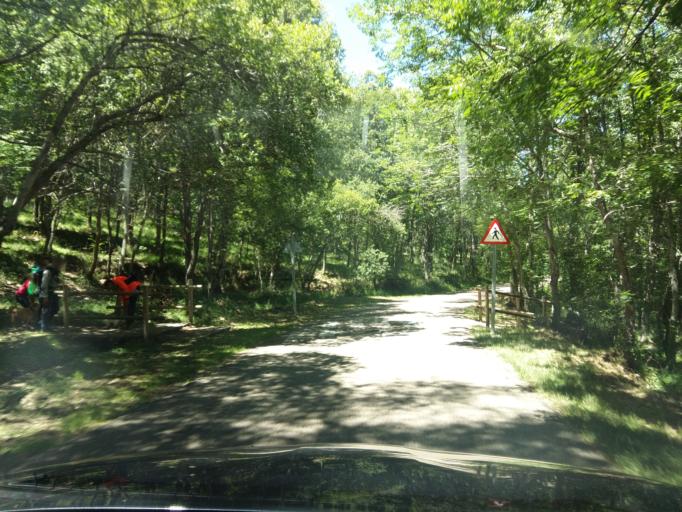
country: ES
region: Castille and Leon
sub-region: Provincia de Soria
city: Vozmediano
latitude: 41.8120
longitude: -1.8208
